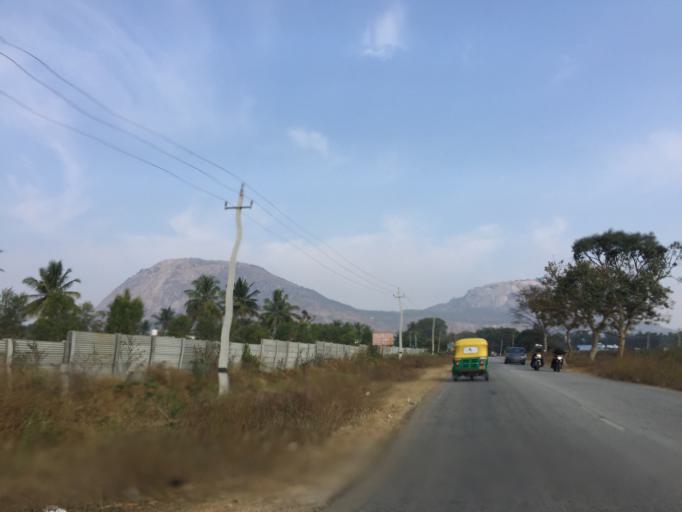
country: IN
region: Karnataka
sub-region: Bangalore Rural
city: Devanhalli
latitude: 13.3369
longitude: 77.6894
